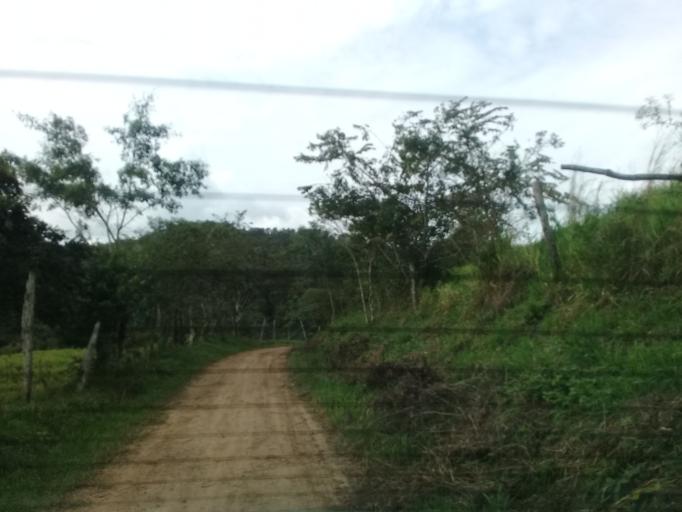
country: CO
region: Cundinamarca
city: Guaduas
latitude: 5.1194
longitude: -74.6073
